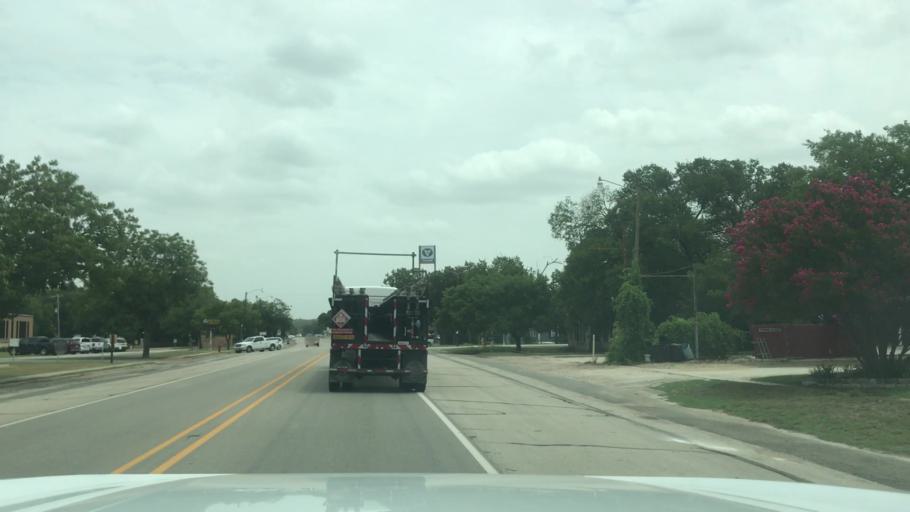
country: US
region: Texas
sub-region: Bosque County
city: Valley Mills
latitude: 31.6605
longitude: -97.4777
